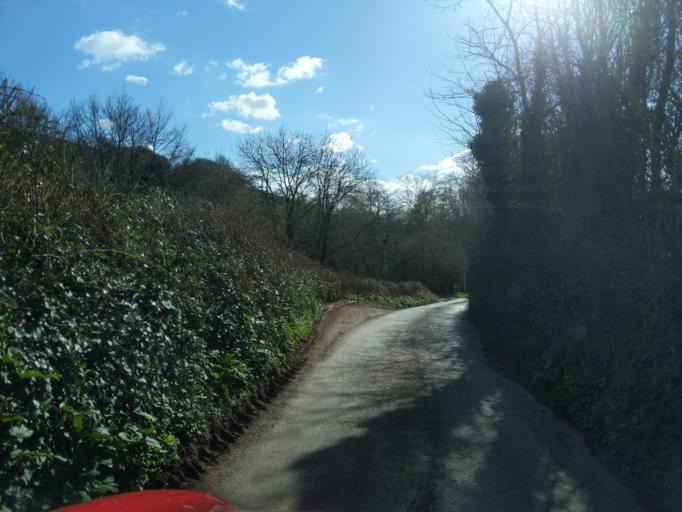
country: GB
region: England
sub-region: Devon
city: Kingsbridge
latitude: 50.2868
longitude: -3.7551
